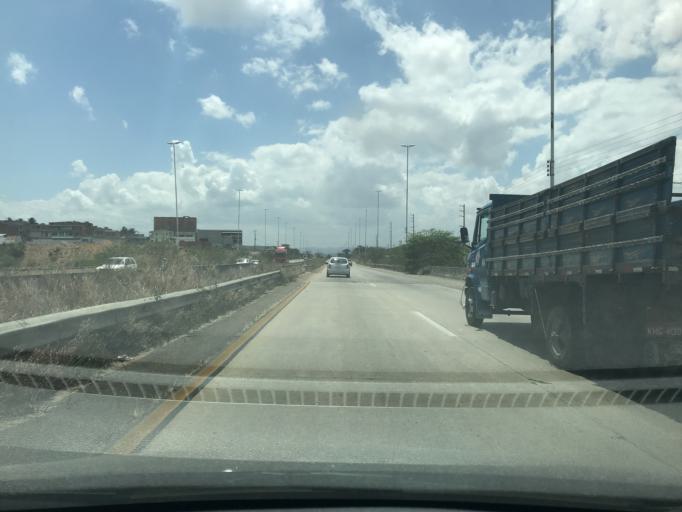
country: BR
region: Pernambuco
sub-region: Caruaru
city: Caruaru
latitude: -8.3042
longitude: -35.9712
